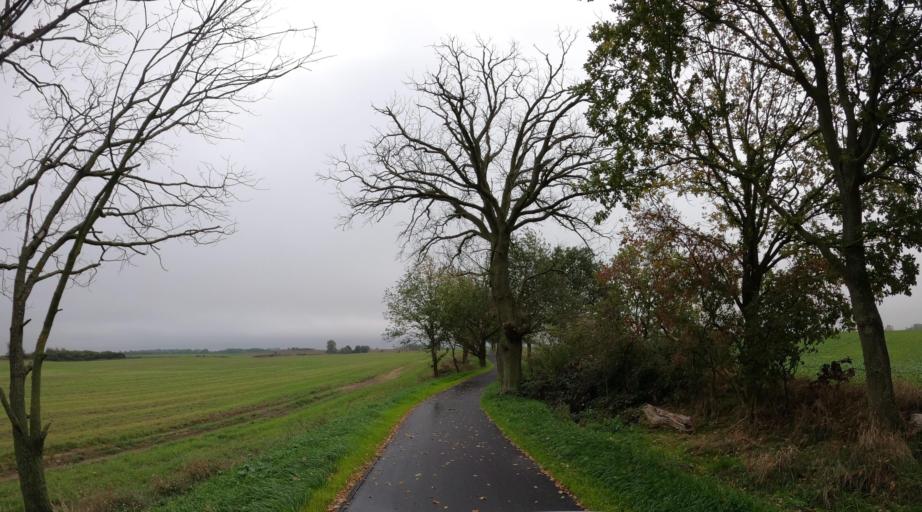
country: PL
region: West Pomeranian Voivodeship
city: Trzcinsko Zdroj
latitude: 52.9298
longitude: 14.7275
